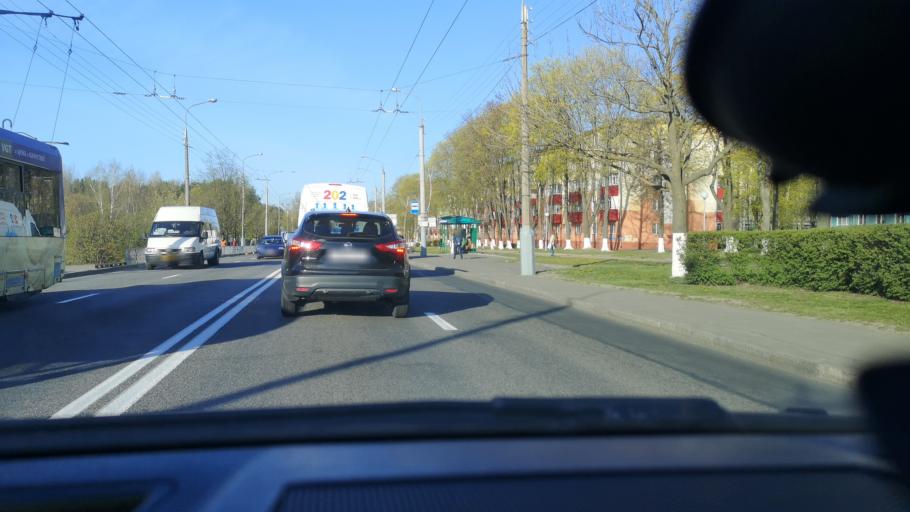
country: BY
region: Gomel
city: Gomel
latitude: 52.4128
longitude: 30.9526
